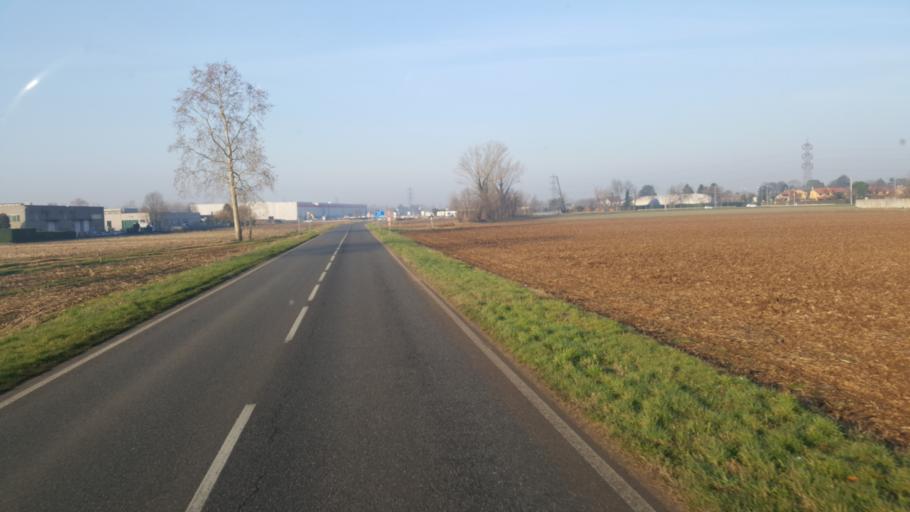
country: IT
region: Lombardy
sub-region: Citta metropolitana di Milano
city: Villaggio Residenziale
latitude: 45.5225
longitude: 9.4718
